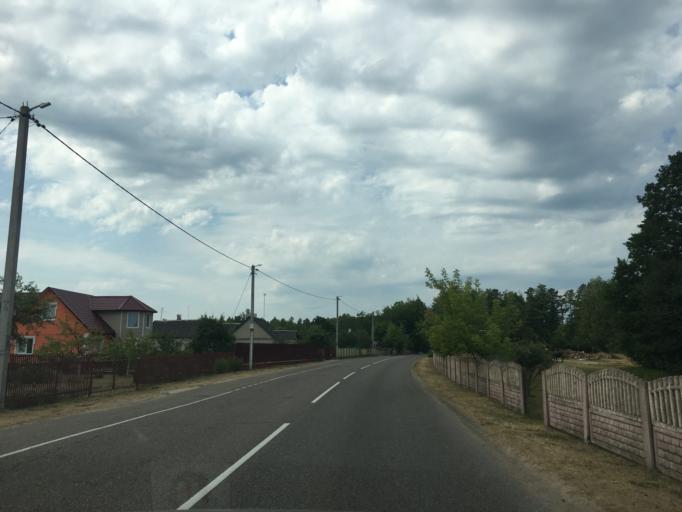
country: LT
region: Alytaus apskritis
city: Druskininkai
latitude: 53.8803
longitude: 24.1298
